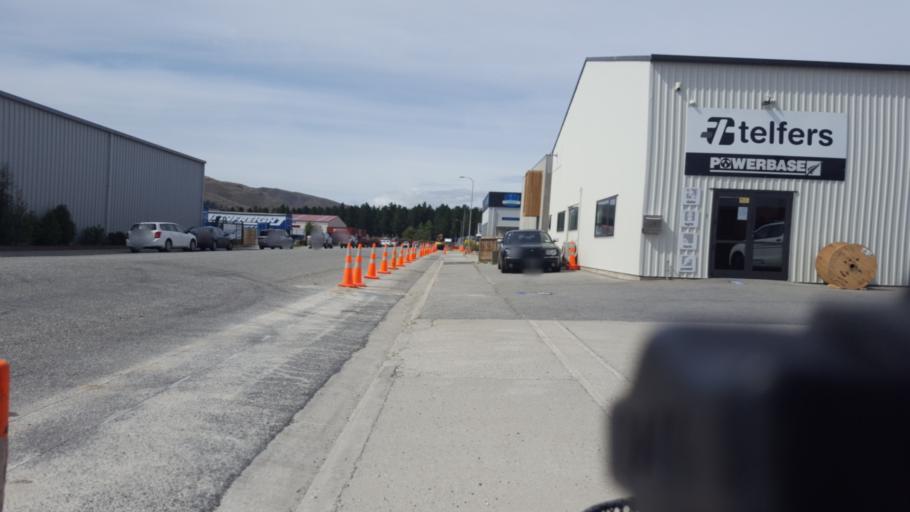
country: NZ
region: Otago
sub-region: Queenstown-Lakes District
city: Wanaka
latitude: -45.0515
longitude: 169.1878
